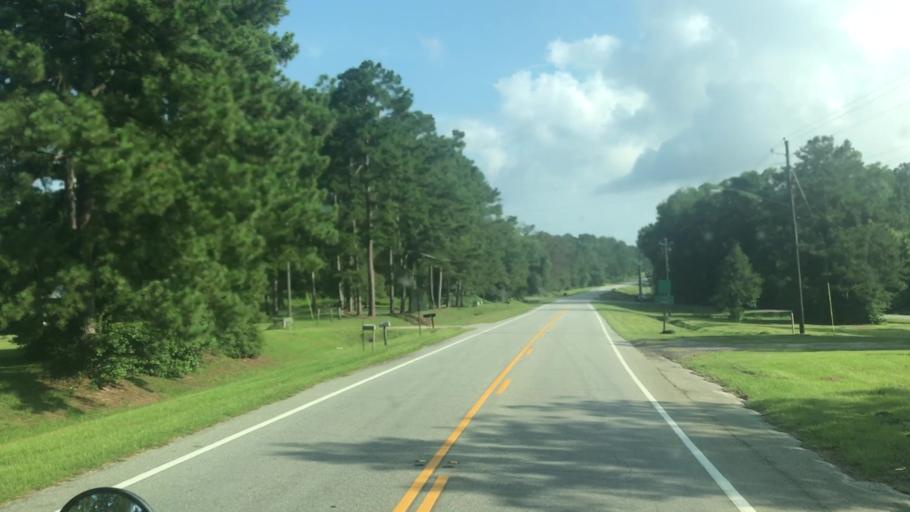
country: US
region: Florida
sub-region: Gadsden County
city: Havana
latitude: 30.7512
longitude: -84.4877
